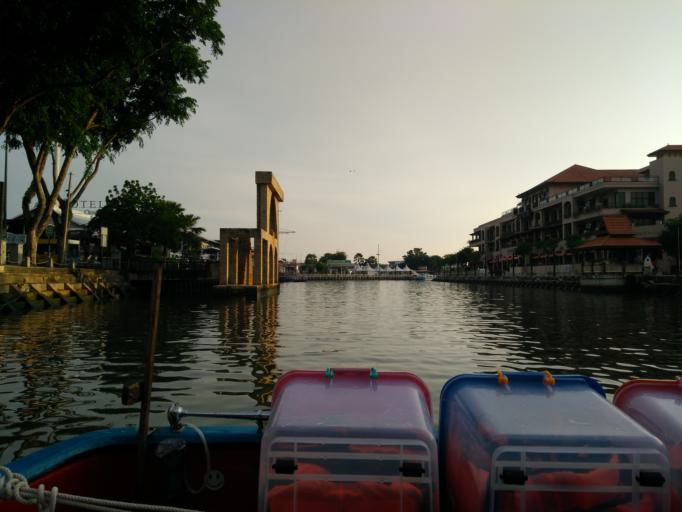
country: MY
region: Melaka
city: Malacca
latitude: 2.1942
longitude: 102.2479
